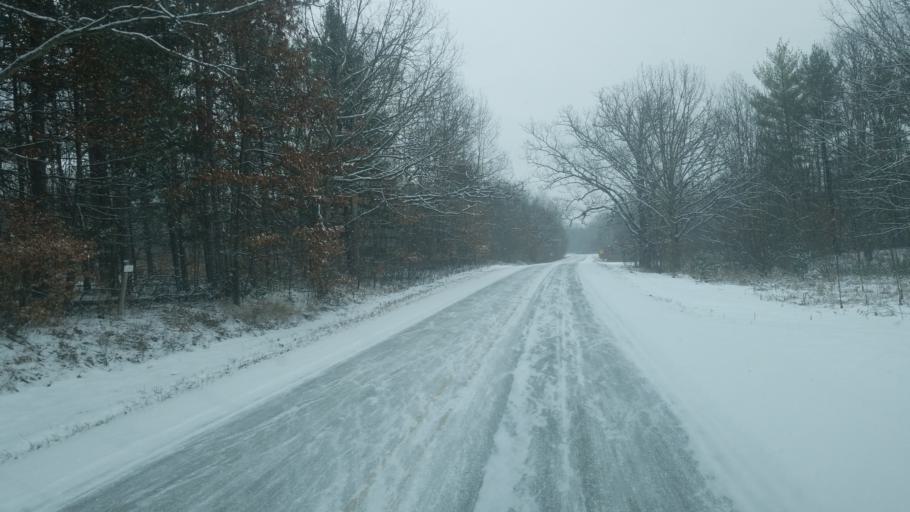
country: US
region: Michigan
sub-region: Mecosta County
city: Big Rapids
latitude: 43.7356
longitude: -85.4096
